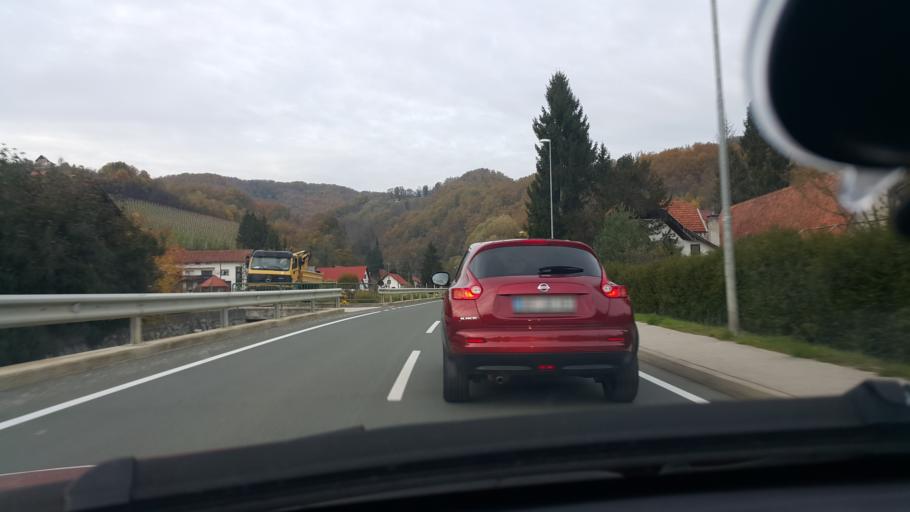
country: SI
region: Bistrica ob Sotli
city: Bistrica ob Sotli
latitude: 46.0207
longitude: 15.6908
